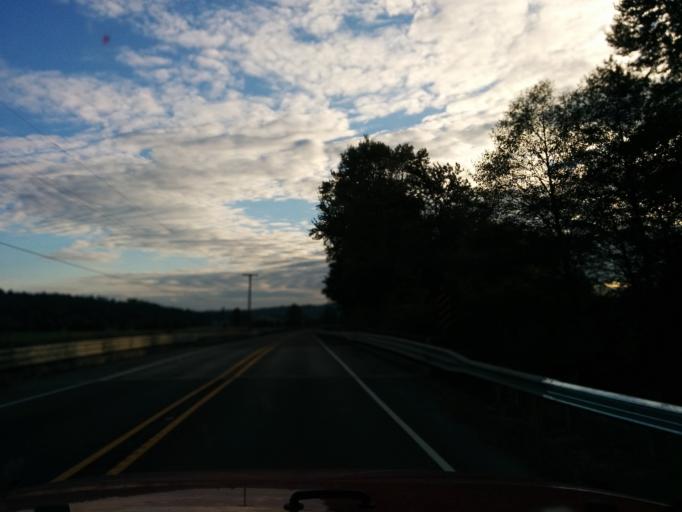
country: US
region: Washington
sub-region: King County
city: Duvall
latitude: 47.7651
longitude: -121.9596
